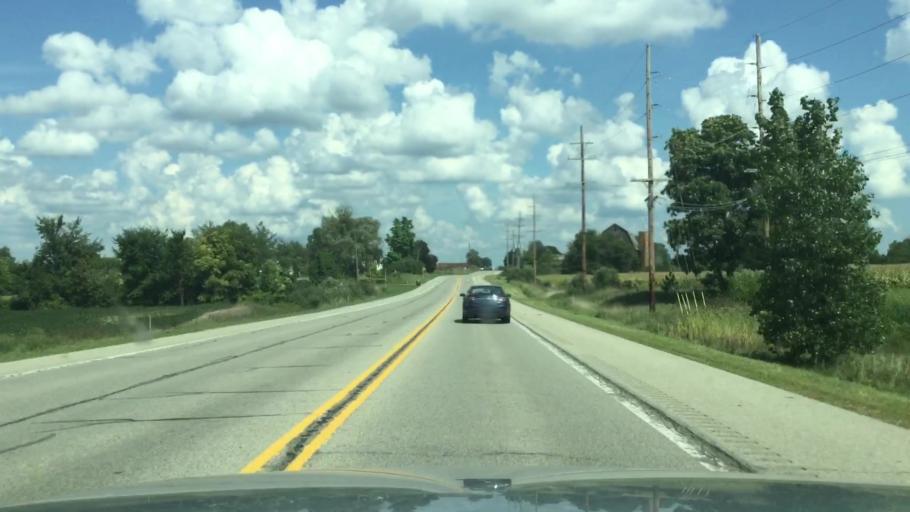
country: US
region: Michigan
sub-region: Washtenaw County
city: Saline
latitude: 42.1407
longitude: -83.8437
